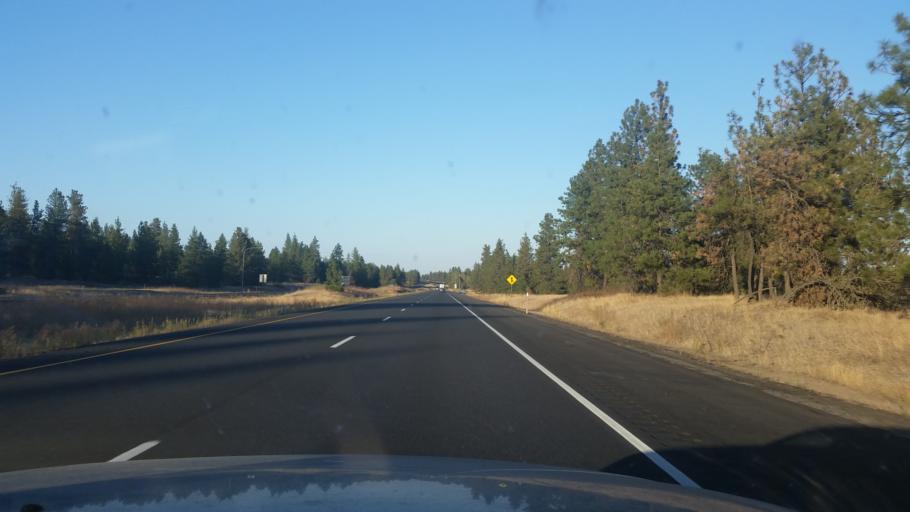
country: US
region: Washington
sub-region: Spokane County
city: Medical Lake
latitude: 47.5044
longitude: -117.6904
